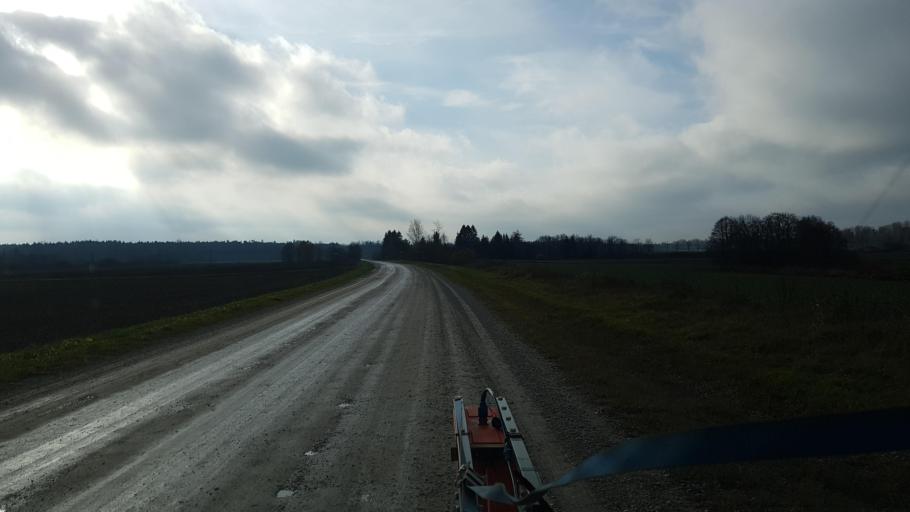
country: EE
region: Raplamaa
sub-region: Maerjamaa vald
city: Marjamaa
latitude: 58.8850
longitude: 24.2389
